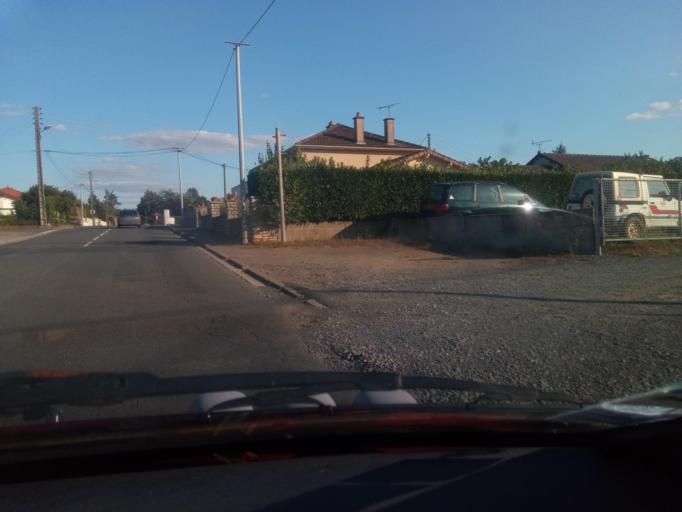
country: FR
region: Poitou-Charentes
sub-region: Departement de la Vienne
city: Availles-Limouzine
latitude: 46.2277
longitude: 0.6879
